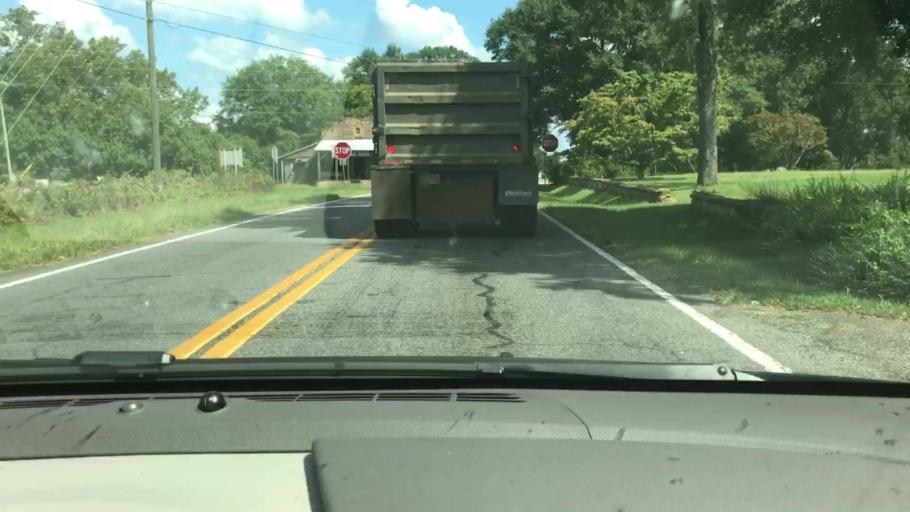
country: US
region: Georgia
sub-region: Troup County
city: West Point
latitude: 32.8689
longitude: -85.0351
